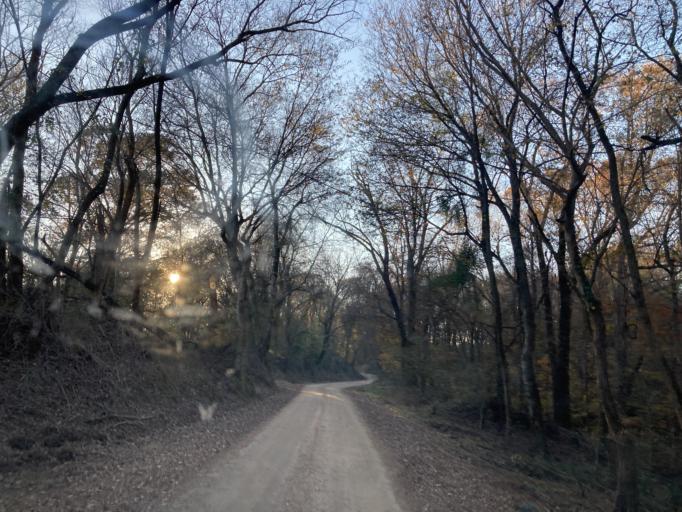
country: US
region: Mississippi
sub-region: Yazoo County
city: Yazoo City
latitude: 32.9508
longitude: -90.2715
